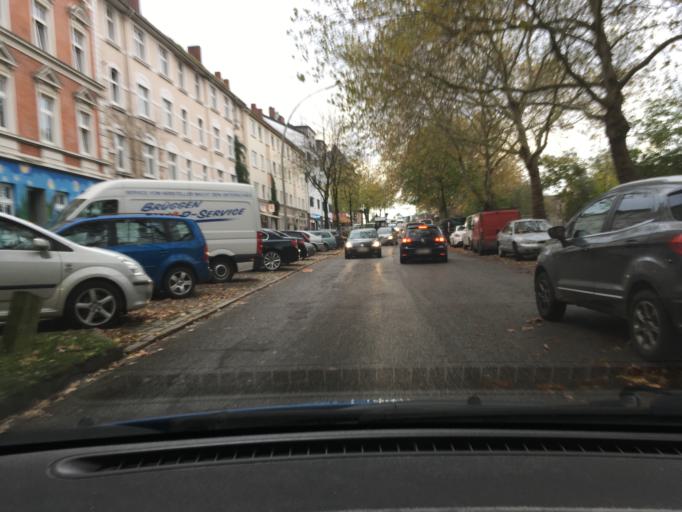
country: DE
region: Hamburg
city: Kleiner Grasbrook
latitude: 53.5018
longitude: 10.0109
